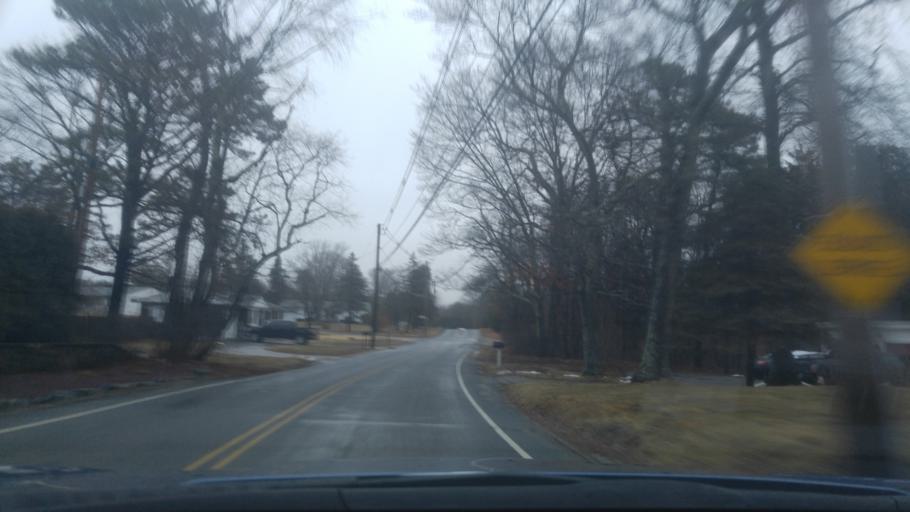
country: US
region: Rhode Island
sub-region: Washington County
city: North Kingstown
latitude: 41.5981
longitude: -71.4854
